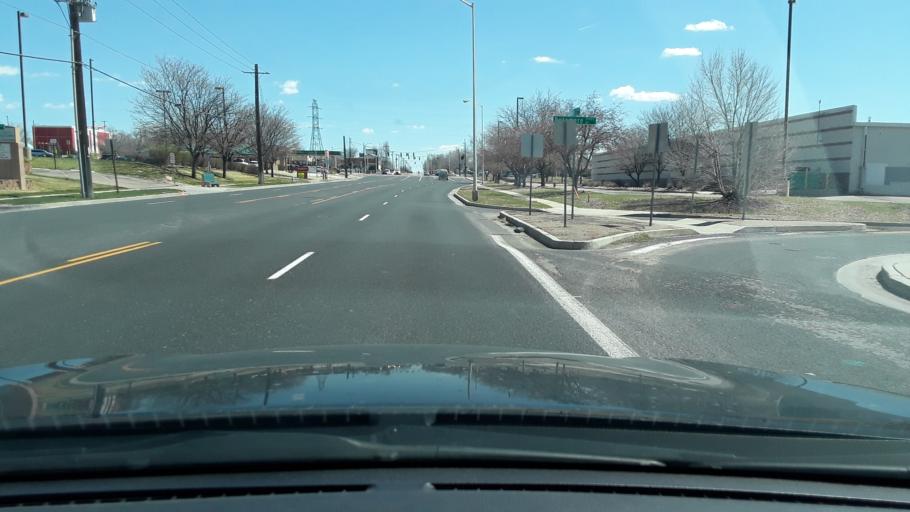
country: US
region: Colorado
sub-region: El Paso County
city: Cimarron Hills
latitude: 38.8470
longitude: -104.7600
